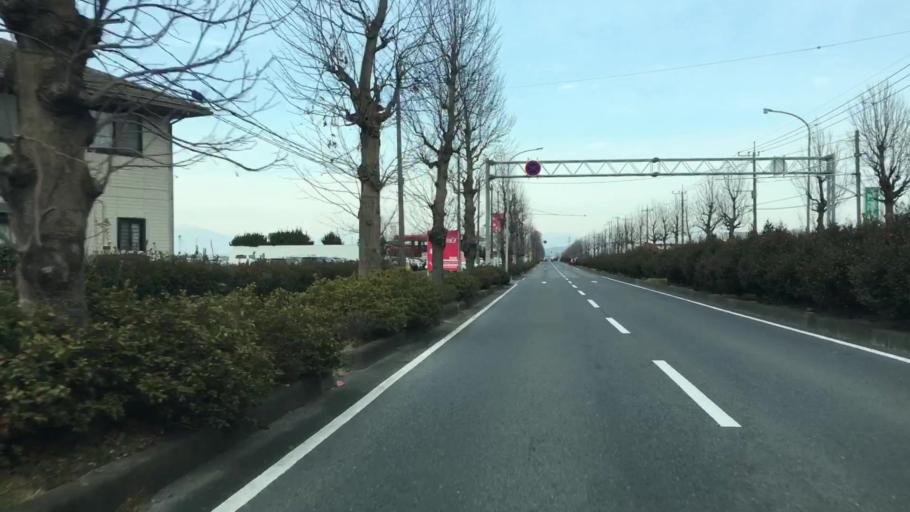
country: JP
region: Saitama
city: Menuma
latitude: 36.1903
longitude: 139.3702
